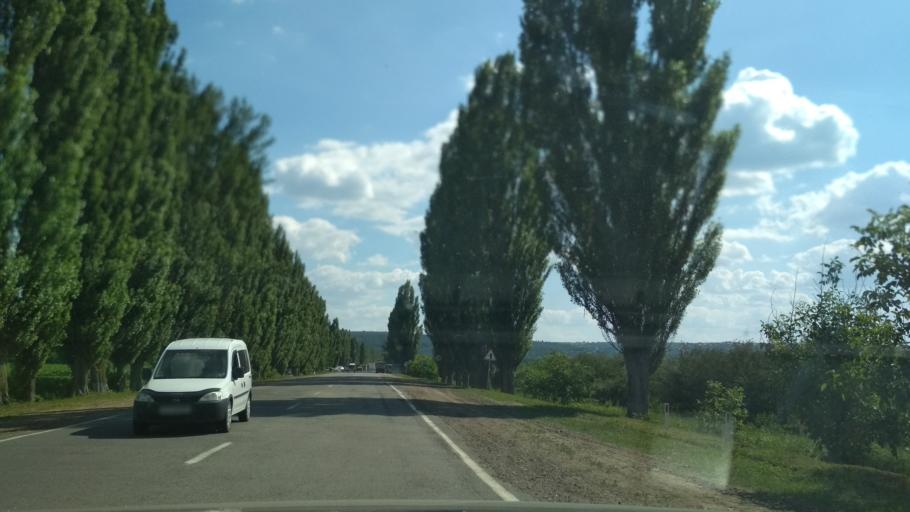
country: MD
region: Chisinau
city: Vadul lui Voda
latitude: 47.1036
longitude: 29.0996
